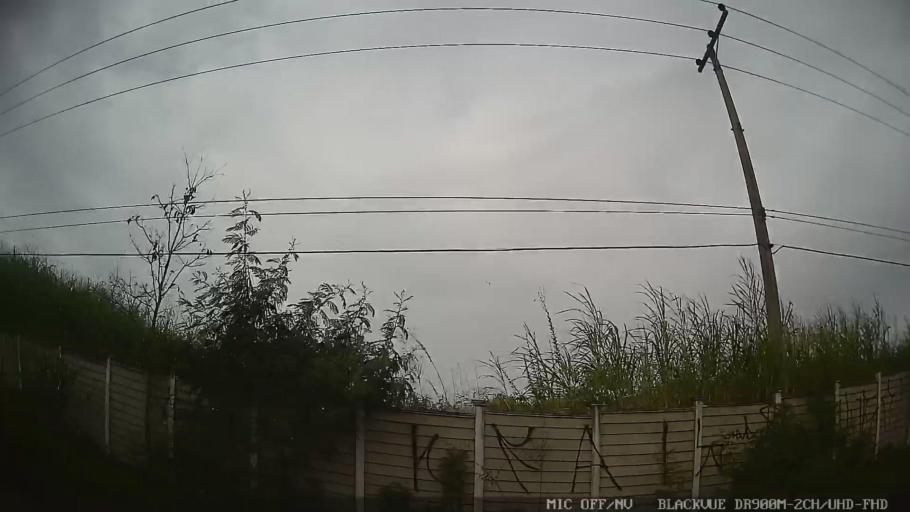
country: BR
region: Sao Paulo
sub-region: Salto
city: Salto
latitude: -23.1871
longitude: -47.2789
